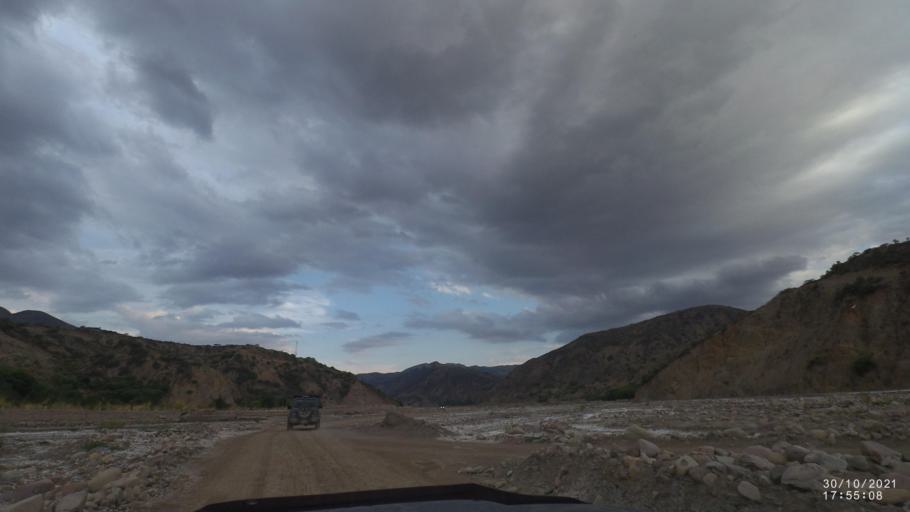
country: BO
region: Cochabamba
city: Sipe Sipe
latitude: -17.5449
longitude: -66.4866
